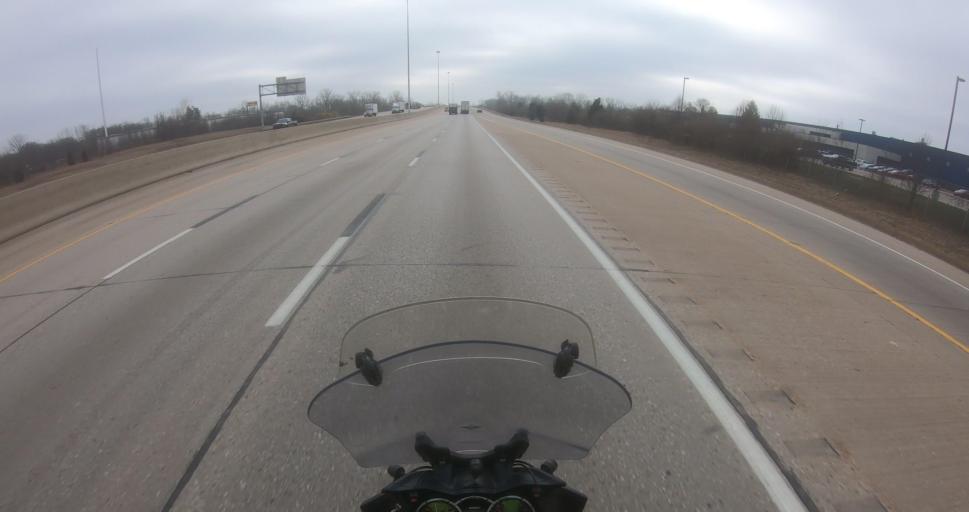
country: US
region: Ohio
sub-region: Miami County
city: Troy
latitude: 40.0218
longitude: -84.2308
